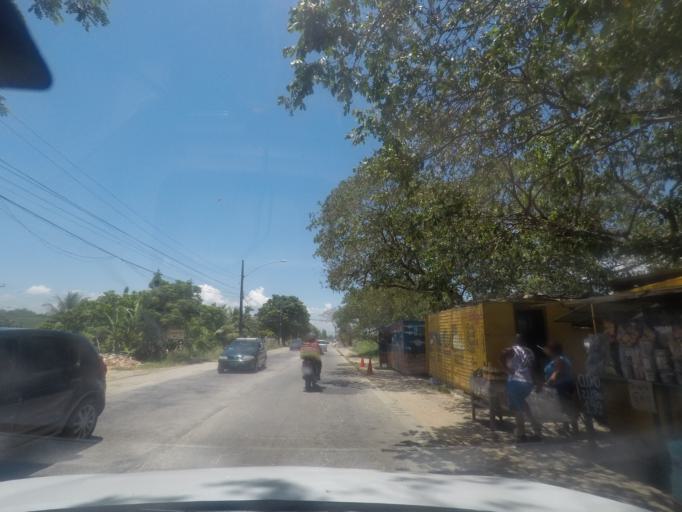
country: BR
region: Rio de Janeiro
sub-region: Itaguai
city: Itaguai
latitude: -22.9064
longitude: -43.6929
